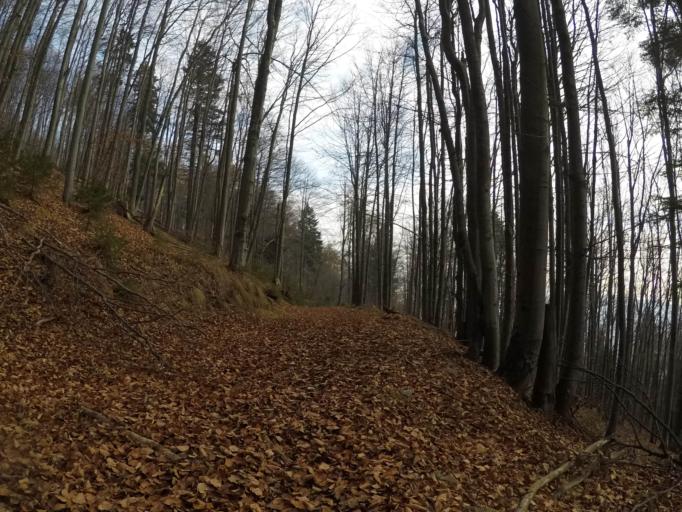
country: SK
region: Kosicky
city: Gelnica
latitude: 48.7744
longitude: 20.9525
